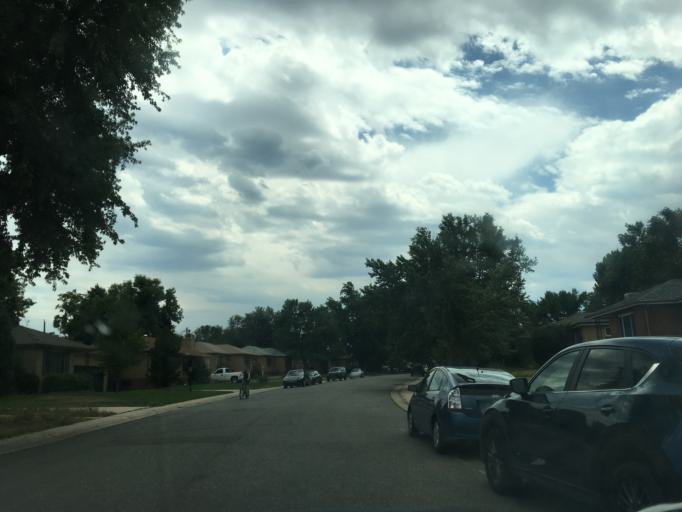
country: US
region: Colorado
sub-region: Arapahoe County
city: Sheridan
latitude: 39.6737
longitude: -105.0491
